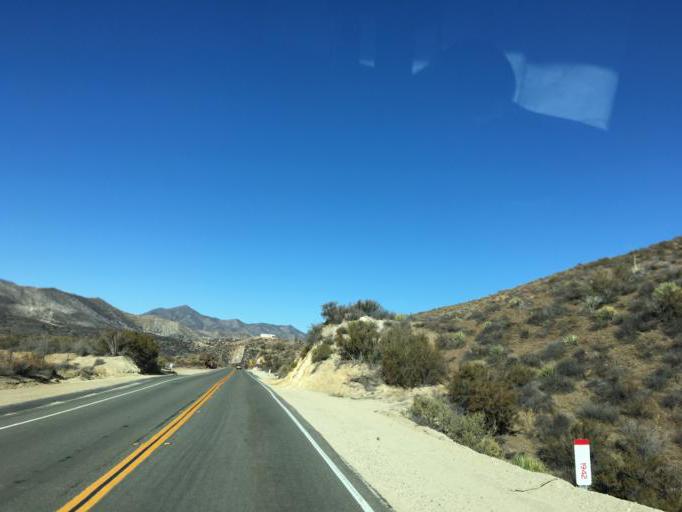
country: US
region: California
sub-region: Los Angeles County
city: Acton
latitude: 34.4392
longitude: -118.2420
